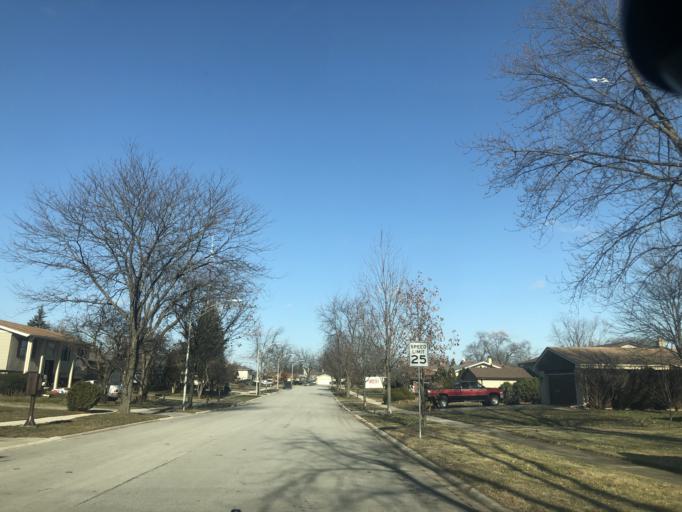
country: US
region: Illinois
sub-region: DuPage County
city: Addison
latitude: 41.9235
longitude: -88.0059
